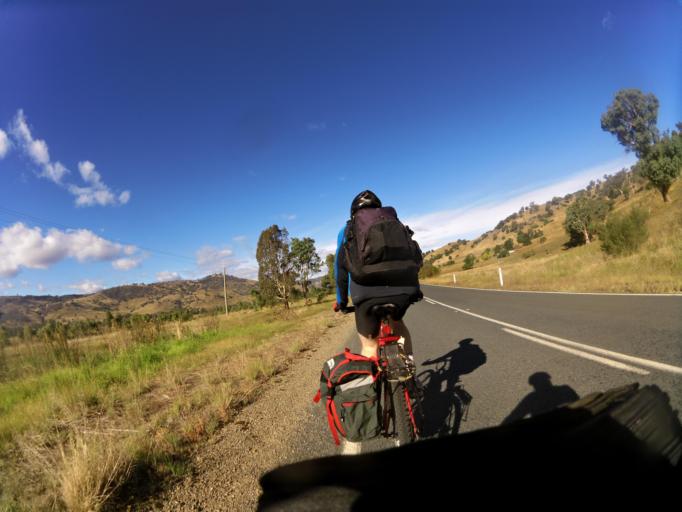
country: AU
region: New South Wales
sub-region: Greater Hume Shire
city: Holbrook
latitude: -35.9644
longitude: 147.7476
